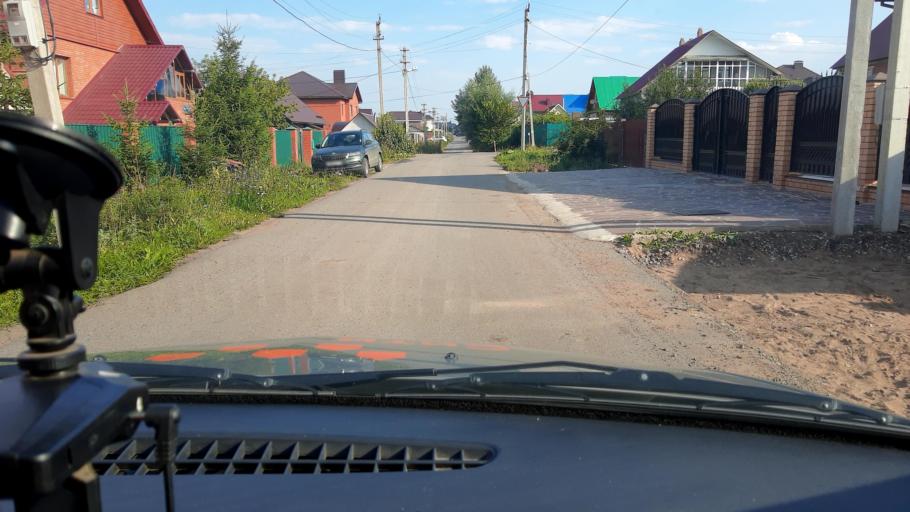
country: RU
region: Bashkortostan
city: Ufa
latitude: 54.5967
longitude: 55.9311
